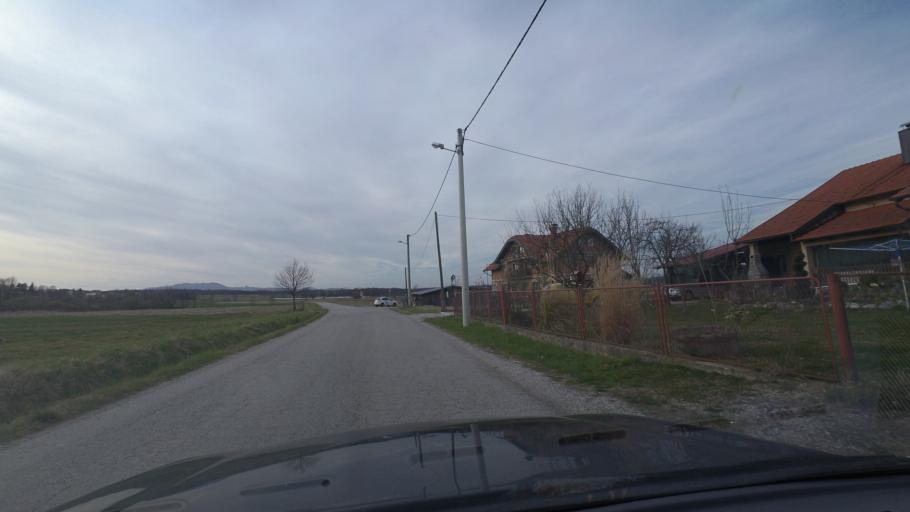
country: HR
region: Grad Zagreb
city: Horvati
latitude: 45.6893
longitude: 15.8503
